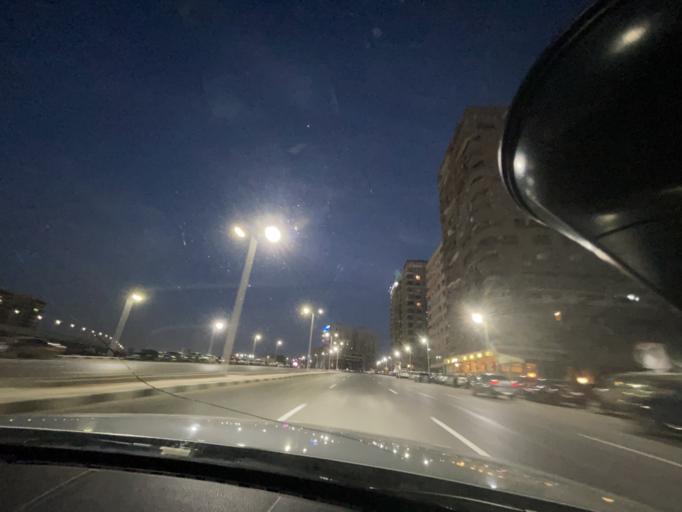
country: EG
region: Muhafazat al Qahirah
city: Cairo
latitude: 30.0690
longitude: 31.3523
